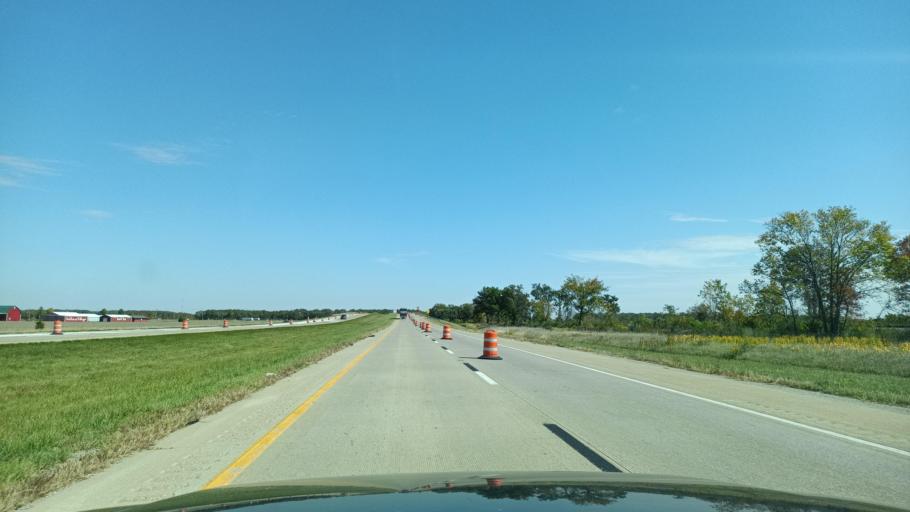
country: US
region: Ohio
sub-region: Defiance County
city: Defiance
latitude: 41.2595
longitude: -84.4449
